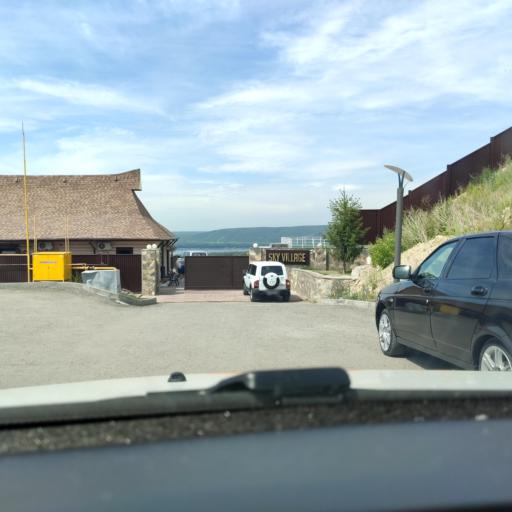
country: RU
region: Samara
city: Volzhskiy
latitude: 53.3394
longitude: 50.1988
